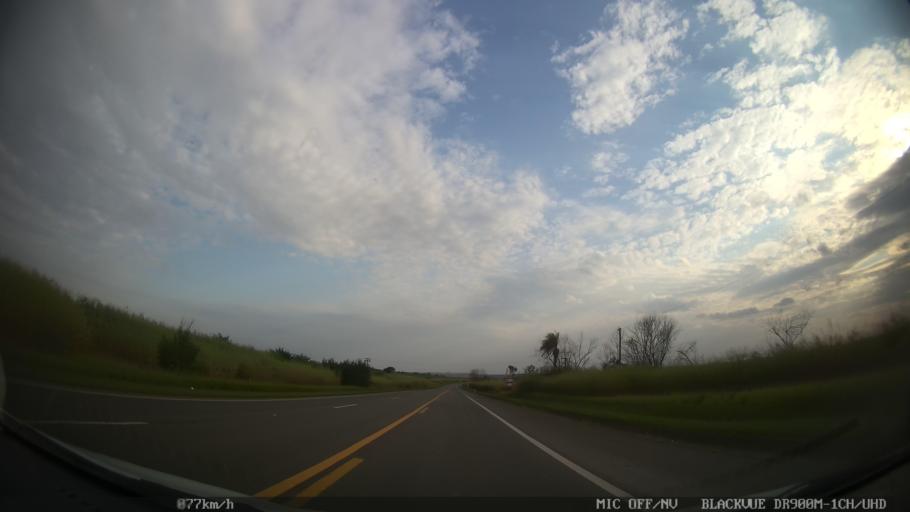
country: BR
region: Sao Paulo
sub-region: Cosmopolis
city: Cosmopolis
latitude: -22.6235
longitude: -47.2560
